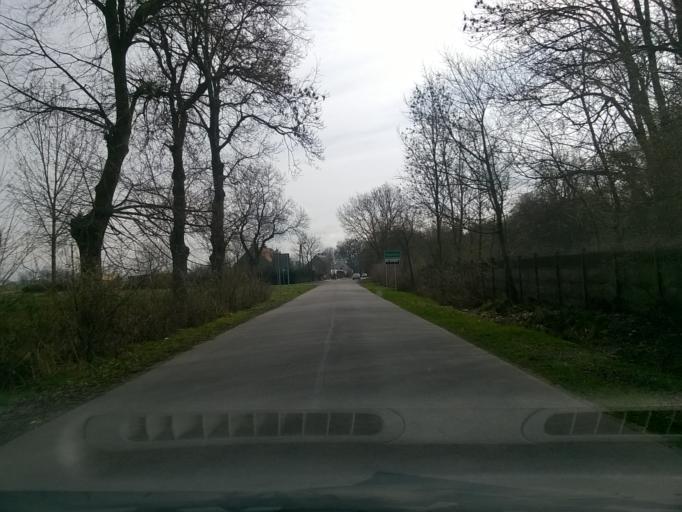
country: PL
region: Kujawsko-Pomorskie
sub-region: Powiat nakielski
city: Kcynia
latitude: 52.9901
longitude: 17.4200
